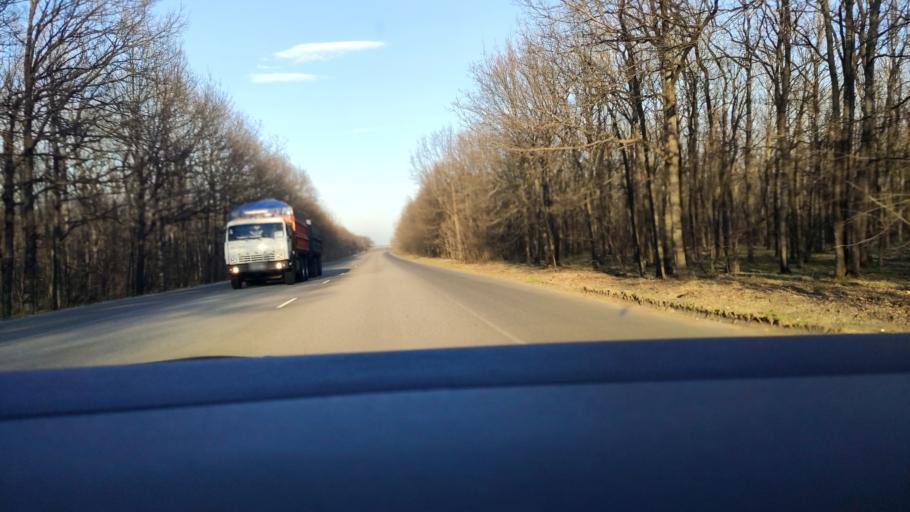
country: RU
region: Voronezj
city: Kolodeznyy
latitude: 51.3392
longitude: 39.0645
